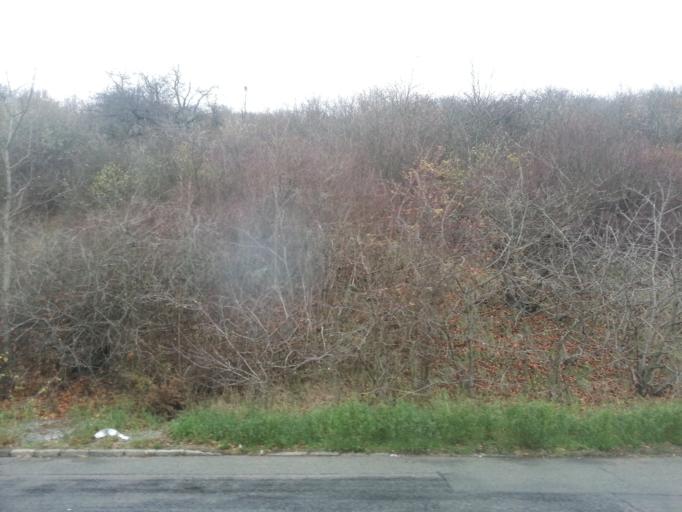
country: CZ
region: Praha
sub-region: Praha 1
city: Mala Strana
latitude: 50.0780
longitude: 14.3801
